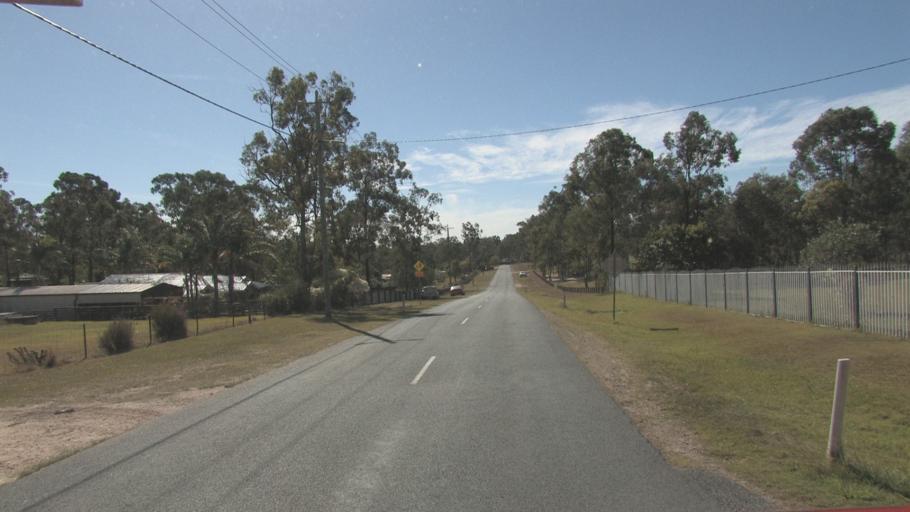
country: AU
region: Queensland
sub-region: Logan
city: North Maclean
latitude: -27.7299
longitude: 152.9614
